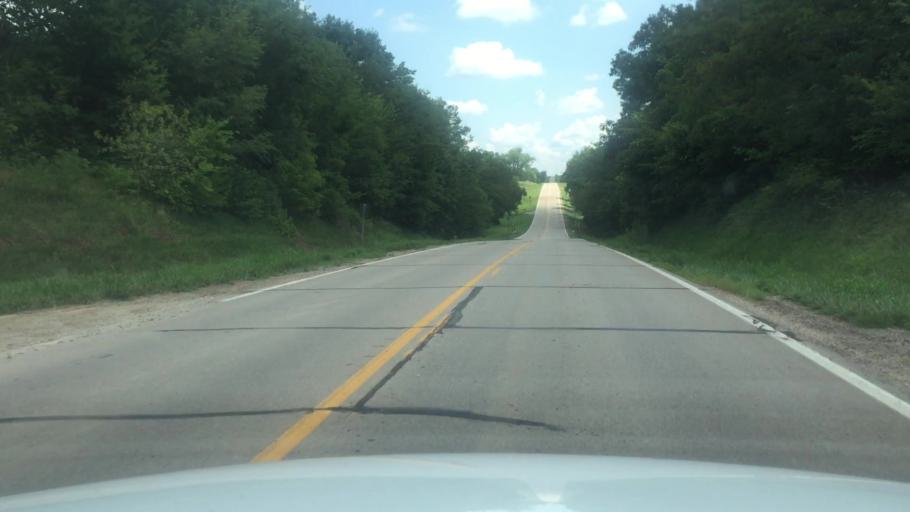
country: US
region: Kansas
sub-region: Brown County
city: Horton
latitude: 39.6674
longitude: -95.6378
